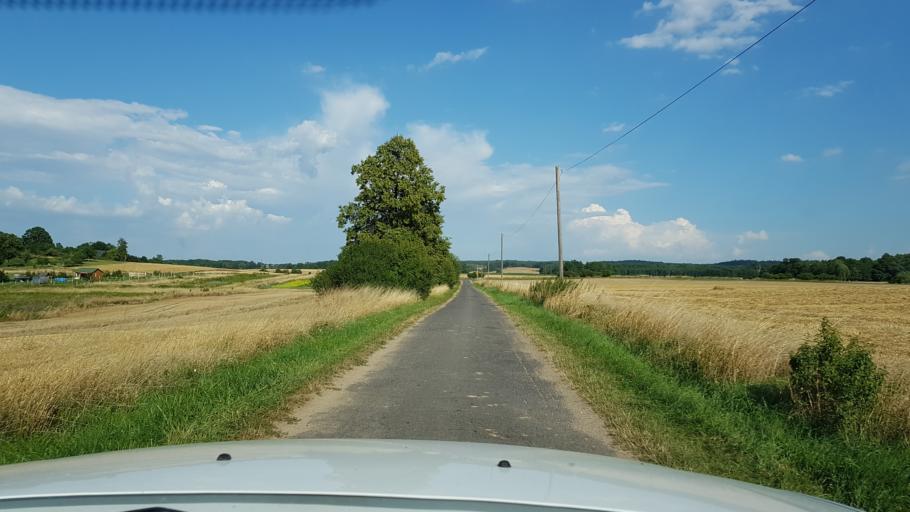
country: PL
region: West Pomeranian Voivodeship
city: Trzcinsko Zdroj
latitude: 52.9318
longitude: 14.5906
